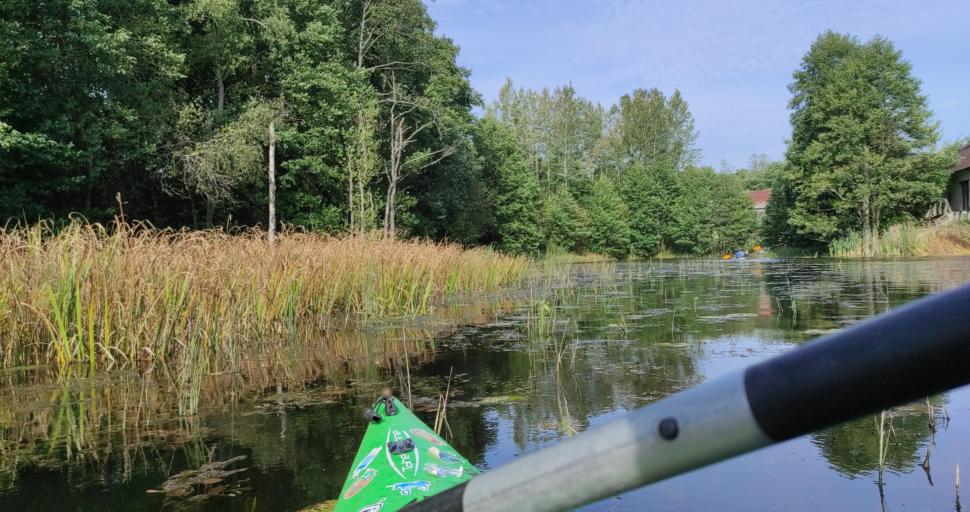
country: LV
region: Kuldigas Rajons
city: Kuldiga
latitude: 57.2421
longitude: 22.0854
